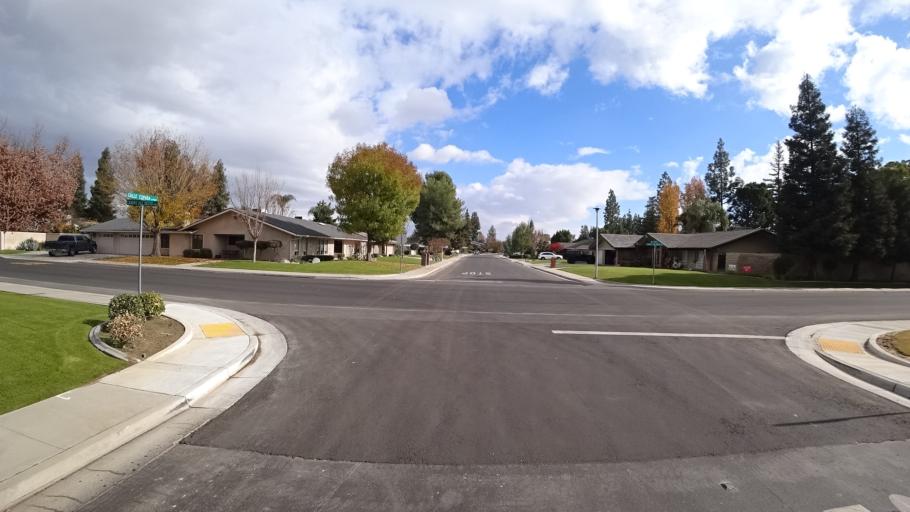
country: US
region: California
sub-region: Kern County
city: Greenacres
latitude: 35.3477
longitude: -119.0905
